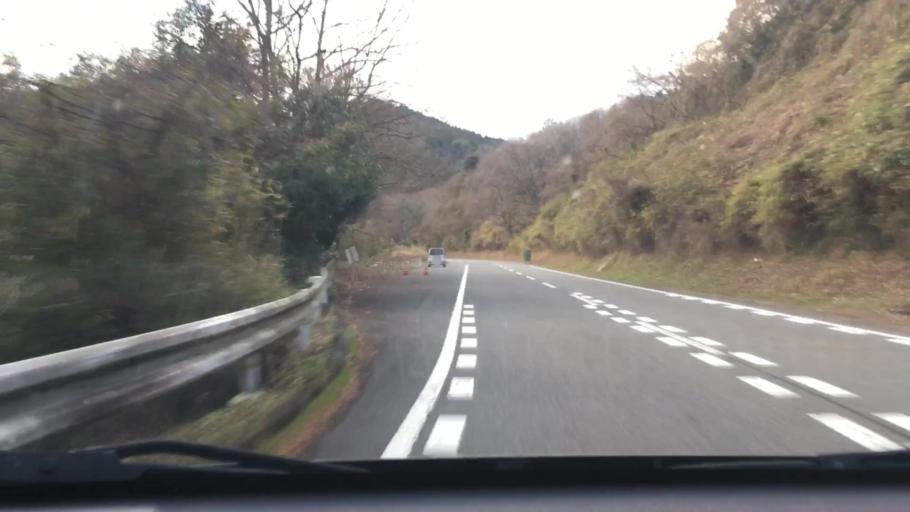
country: JP
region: Oita
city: Hiji
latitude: 33.4134
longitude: 131.4229
